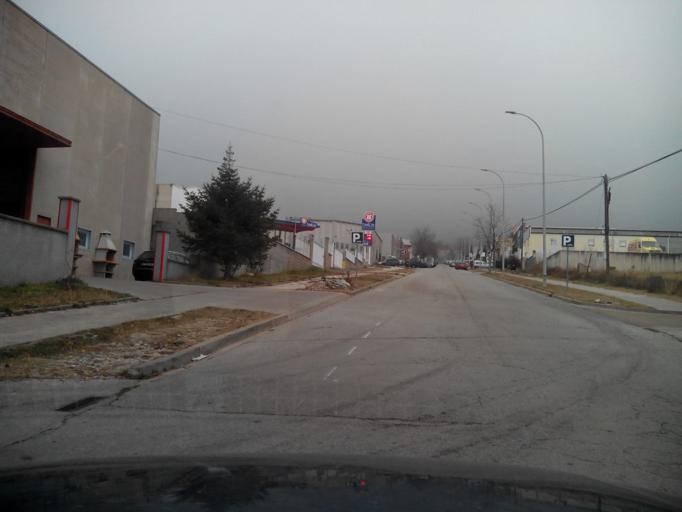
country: ES
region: Catalonia
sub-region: Provincia de Barcelona
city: Berga
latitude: 42.0936
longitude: 1.8255
